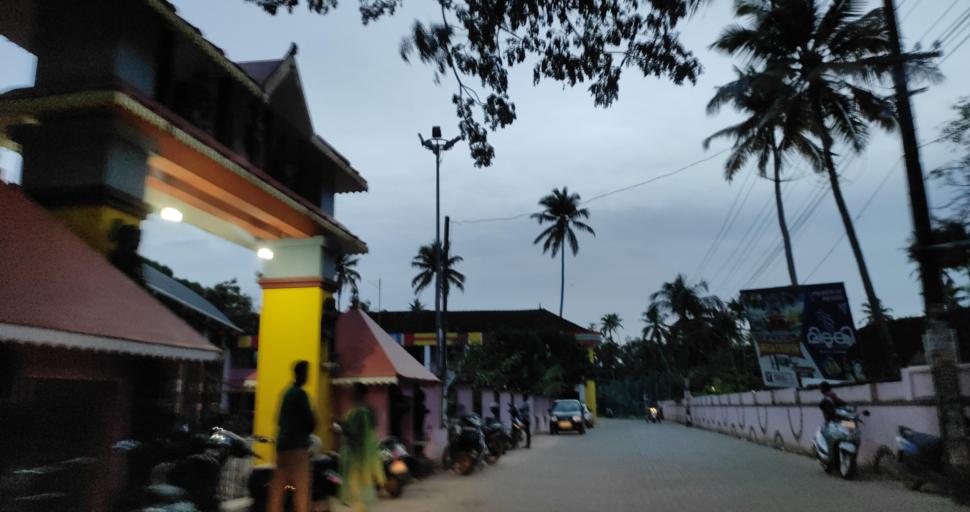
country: IN
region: Kerala
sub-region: Alappuzha
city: Vayalar
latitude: 9.7043
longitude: 76.3060
